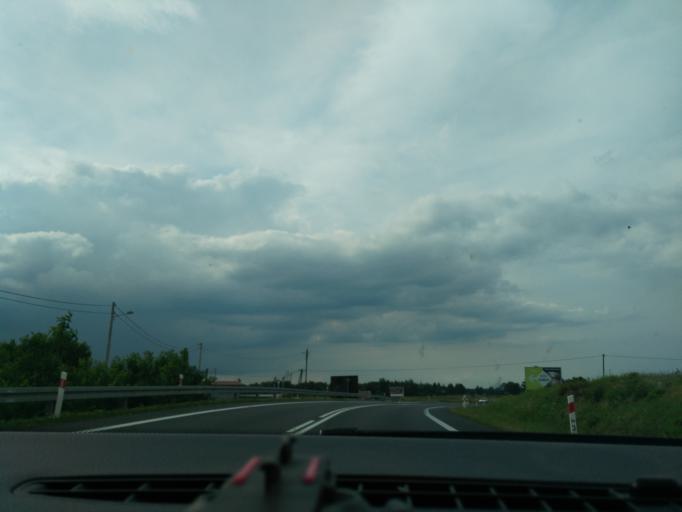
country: PL
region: Subcarpathian Voivodeship
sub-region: Powiat nizanski
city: Jezowe
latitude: 50.3561
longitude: 22.1230
